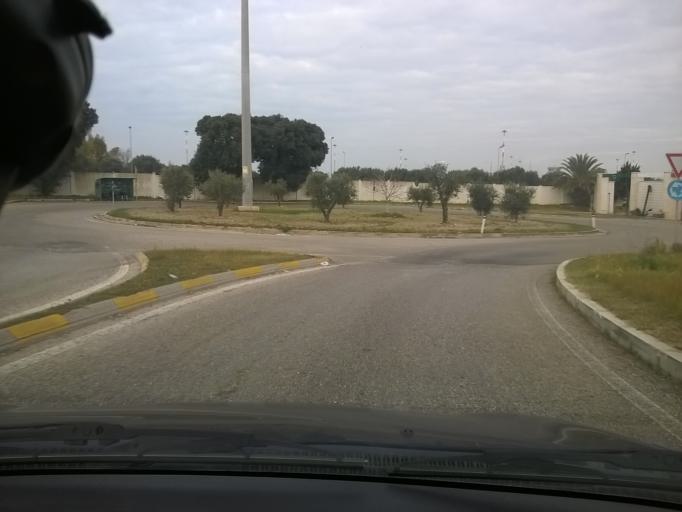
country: IT
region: Apulia
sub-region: Provincia di Taranto
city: Taranto
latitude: 40.4385
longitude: 17.2526
